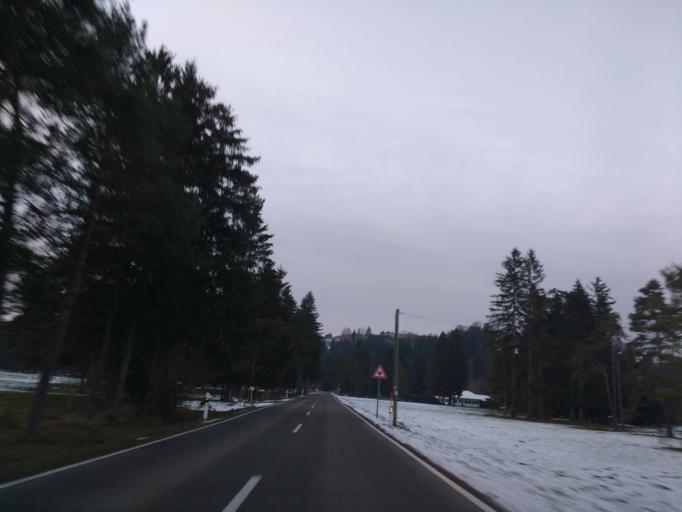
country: DE
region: Bavaria
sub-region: Swabia
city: Halblech
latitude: 47.6452
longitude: 10.8172
